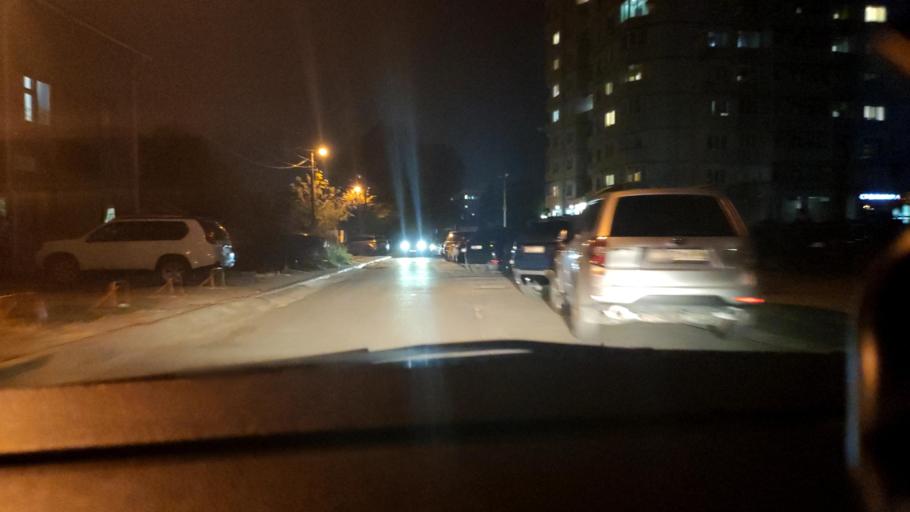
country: RU
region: Voronezj
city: Voronezh
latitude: 51.6791
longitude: 39.1865
